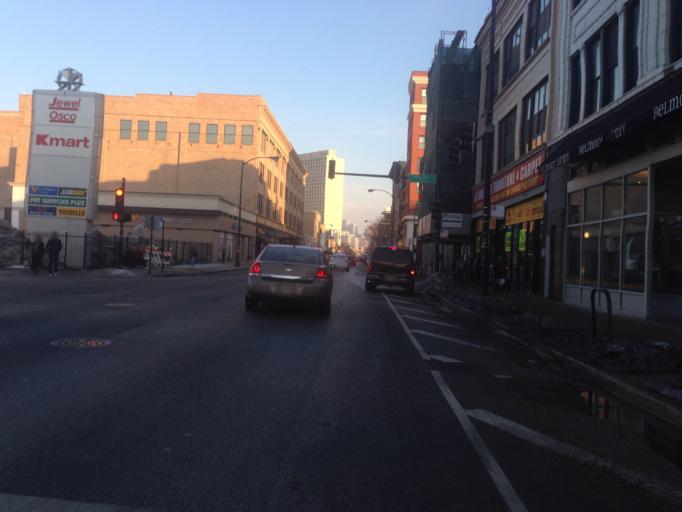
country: US
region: Illinois
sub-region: Cook County
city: Chicago
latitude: 41.9058
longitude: -87.6703
